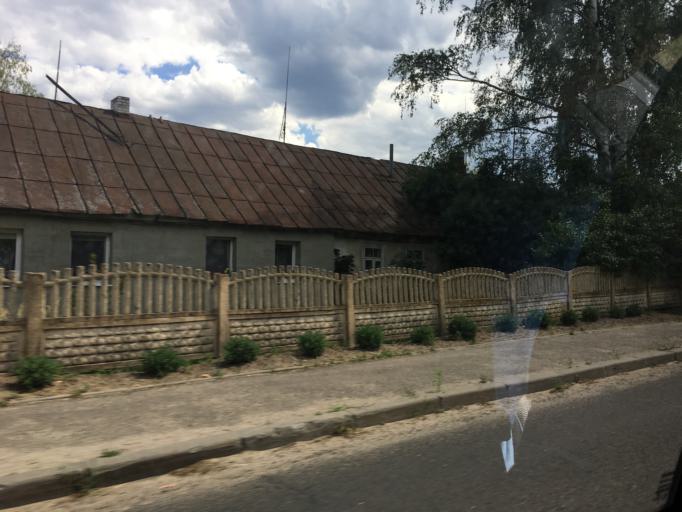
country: LT
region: Alytaus apskritis
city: Druskininkai
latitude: 53.8914
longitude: 24.1411
